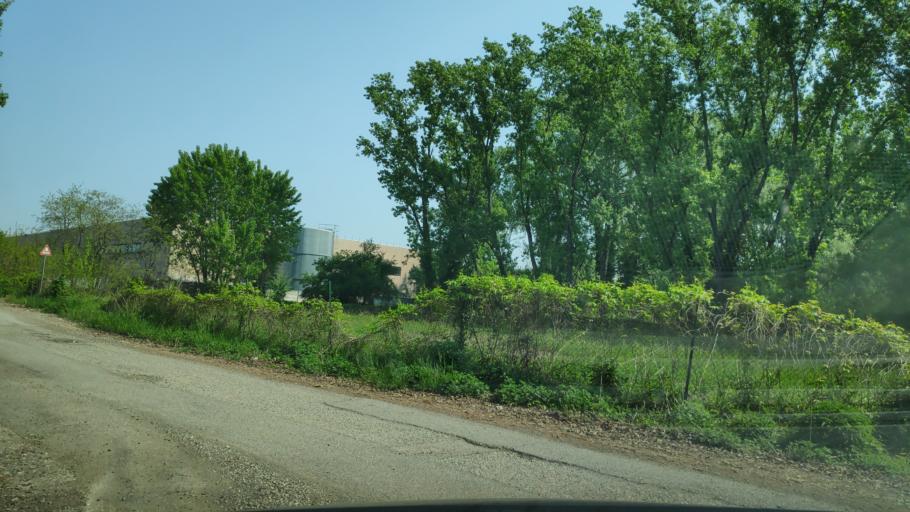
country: IT
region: Lombardy
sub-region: Citta metropolitana di Milano
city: Liscate
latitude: 45.4790
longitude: 9.3963
